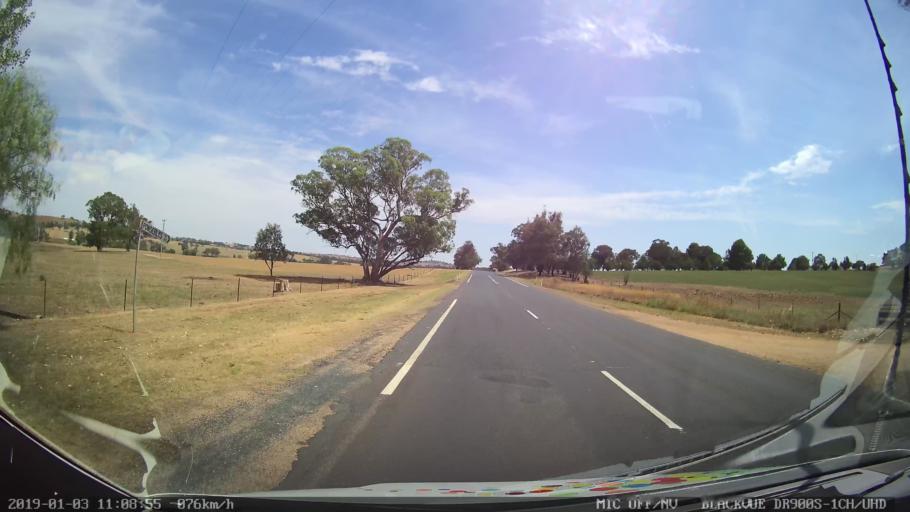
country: AU
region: New South Wales
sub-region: Young
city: Young
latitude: -34.2443
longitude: 148.2556
